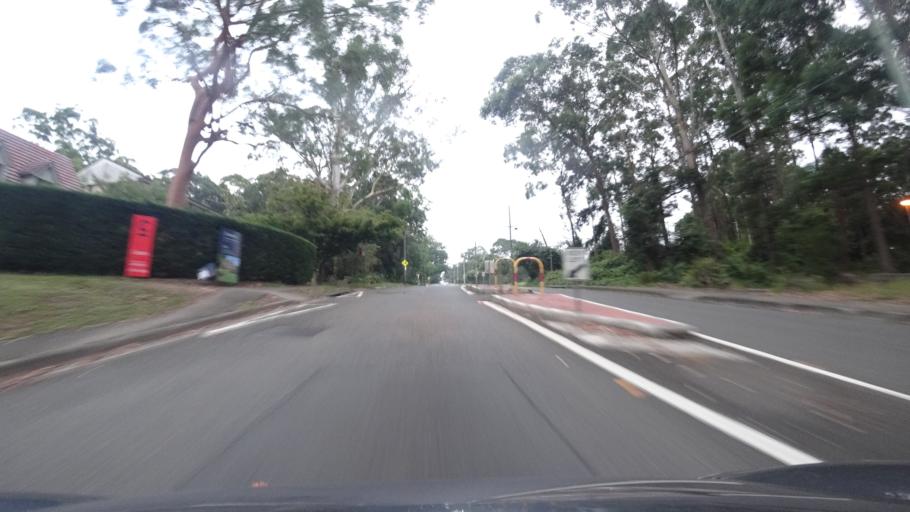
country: AU
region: New South Wales
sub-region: Ryde
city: Macquarie Park
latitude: -33.7650
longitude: 151.1316
